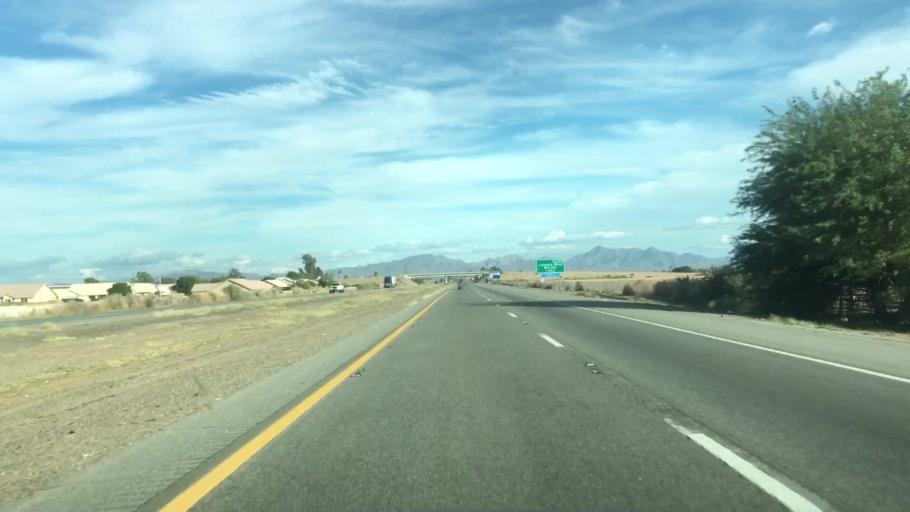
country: US
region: California
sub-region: Riverside County
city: Blythe
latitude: 33.6066
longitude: -114.6305
